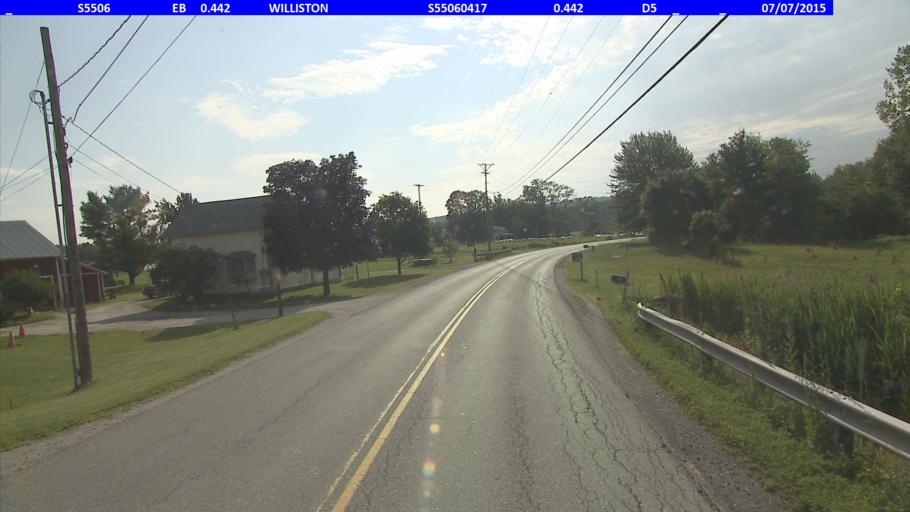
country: US
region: Vermont
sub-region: Chittenden County
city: Essex Junction
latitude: 44.4654
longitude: -73.1043
